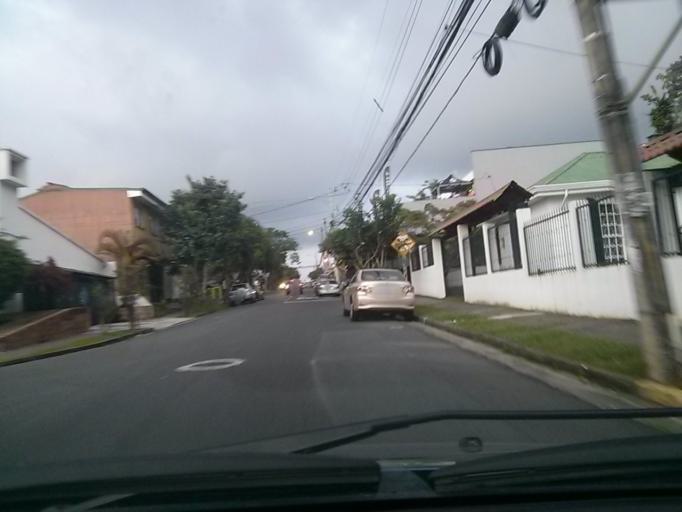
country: CR
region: San Jose
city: San Pedro
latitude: 9.9266
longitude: -84.0396
